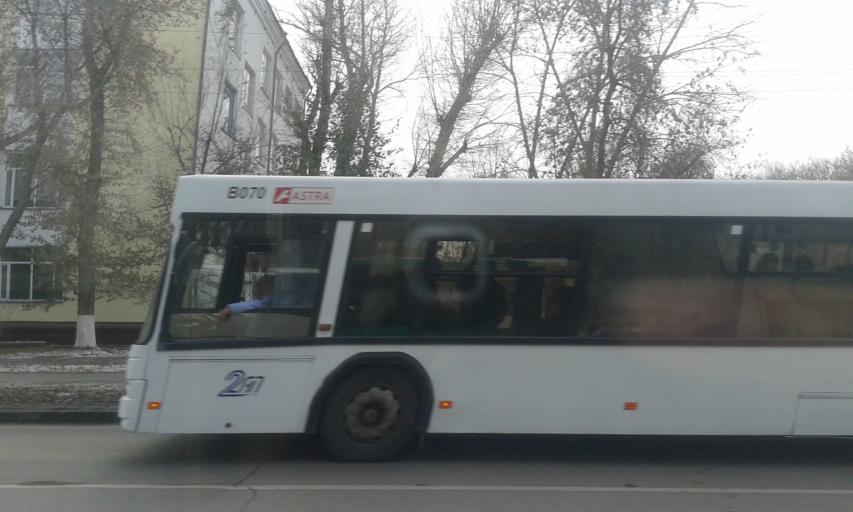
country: KZ
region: Astana Qalasy
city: Astana
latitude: 51.1670
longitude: 71.4496
